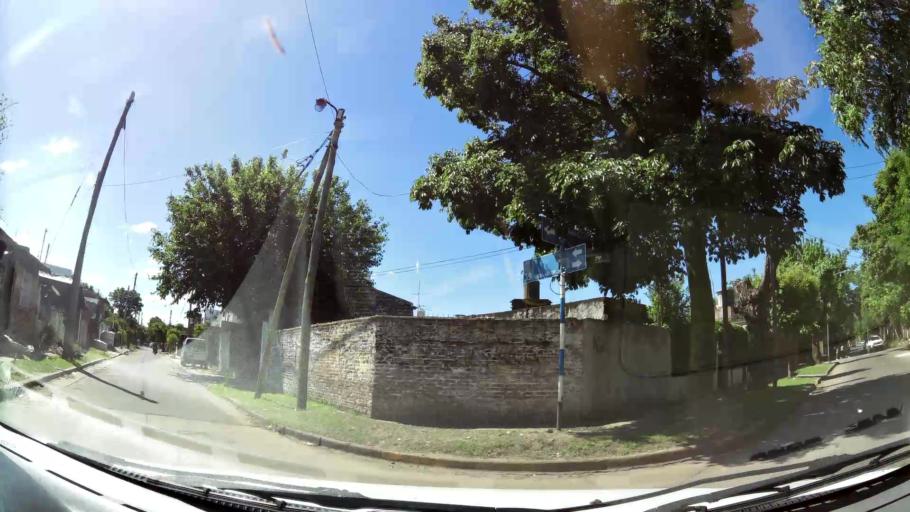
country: AR
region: Buenos Aires
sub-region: Partido de General San Martin
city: General San Martin
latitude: -34.5288
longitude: -58.5654
